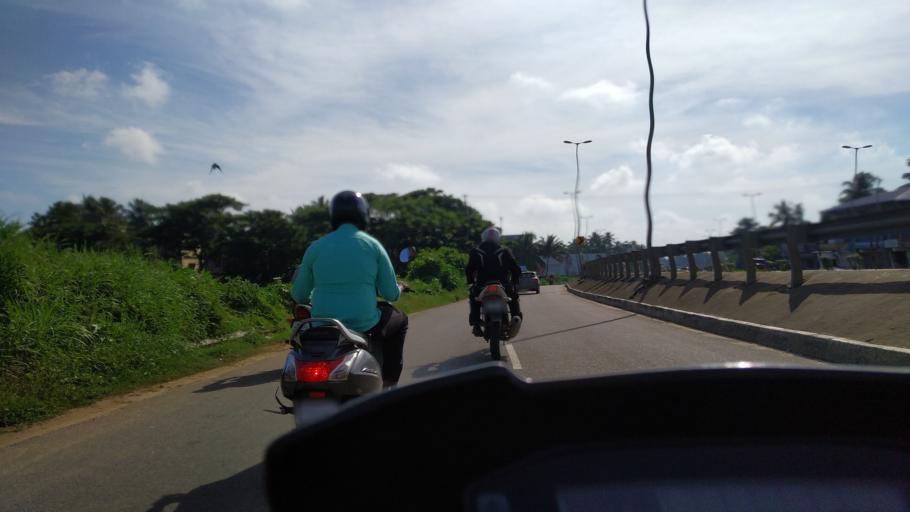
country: IN
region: Kerala
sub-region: Palakkad district
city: Palakkad
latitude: 10.6462
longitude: 76.5474
